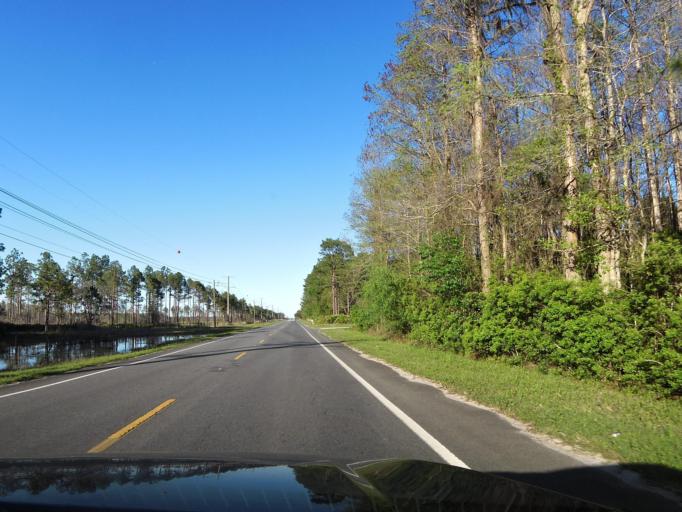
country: US
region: Florida
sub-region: Clay County
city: Keystone Heights
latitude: 29.8642
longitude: -81.9422
